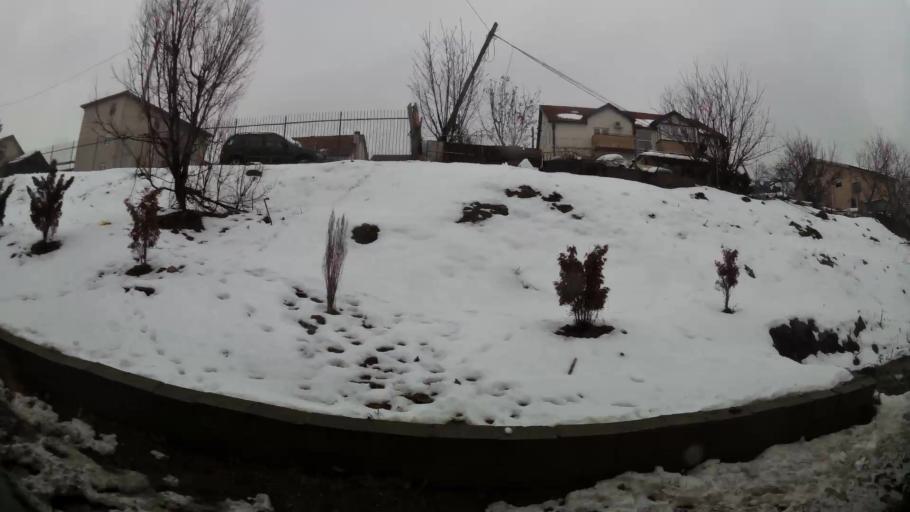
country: RS
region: Central Serbia
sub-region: Belgrade
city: Zemun
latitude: 44.8469
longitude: 20.3788
